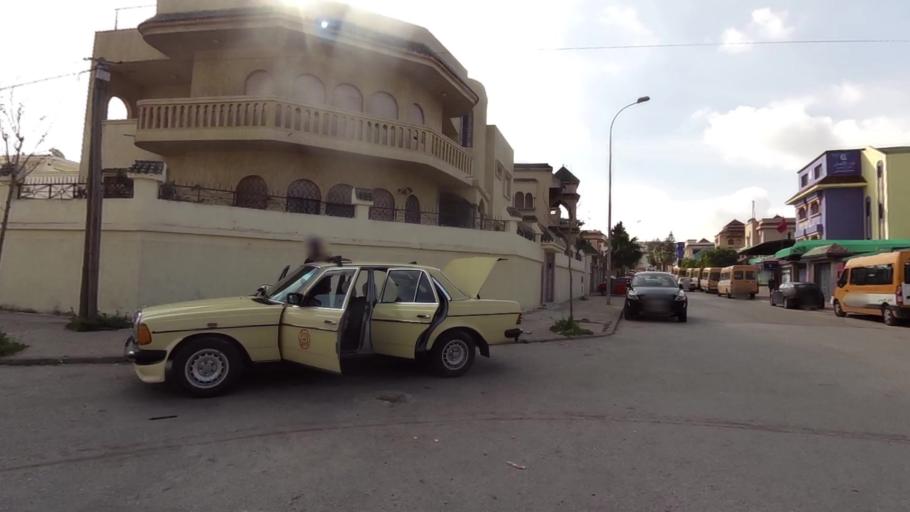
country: MA
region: Tanger-Tetouan
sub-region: Tanger-Assilah
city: Tangier
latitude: 35.7705
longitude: -5.7999
